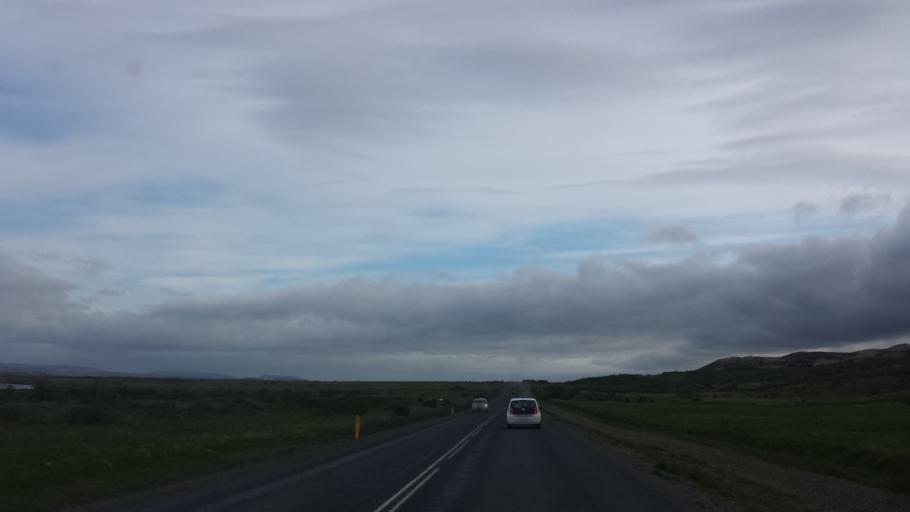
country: IS
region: South
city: Selfoss
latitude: 64.2954
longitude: -20.3345
